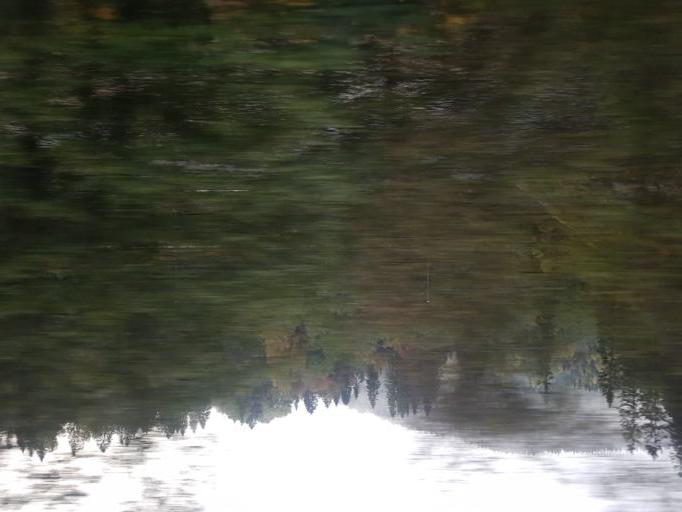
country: NO
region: Sor-Trondelag
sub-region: Midtre Gauldal
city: Storen
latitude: 63.0541
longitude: 10.2884
